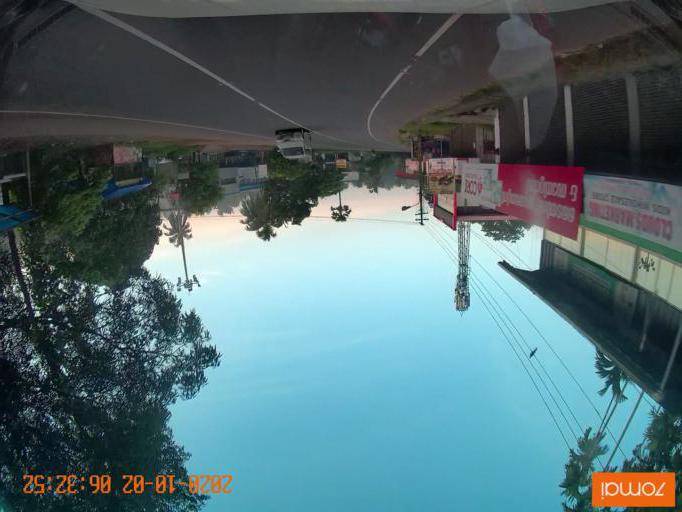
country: IN
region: Kerala
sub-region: Malappuram
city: Ponnani
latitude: 10.7560
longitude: 76.0205
